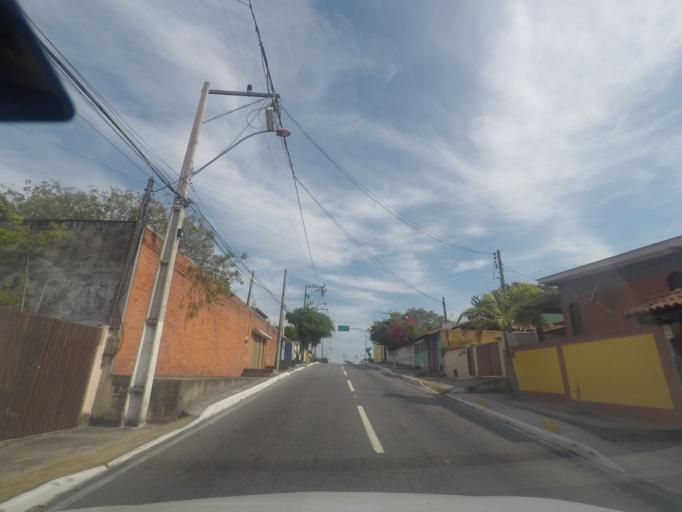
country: BR
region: Rio de Janeiro
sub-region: Marica
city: Marica
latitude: -22.9587
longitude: -42.8148
